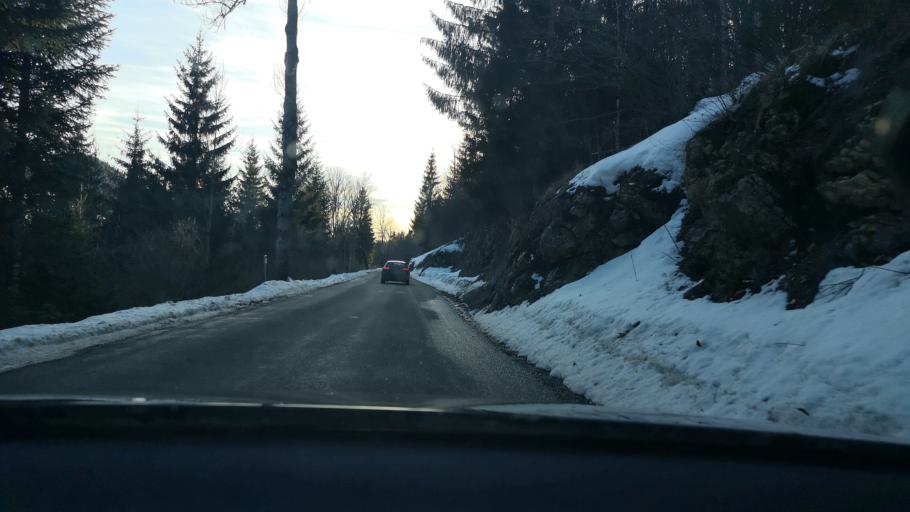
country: FR
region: Franche-Comte
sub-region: Departement du Doubs
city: La Cluse-et-Mijoux
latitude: 46.9293
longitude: 6.4116
